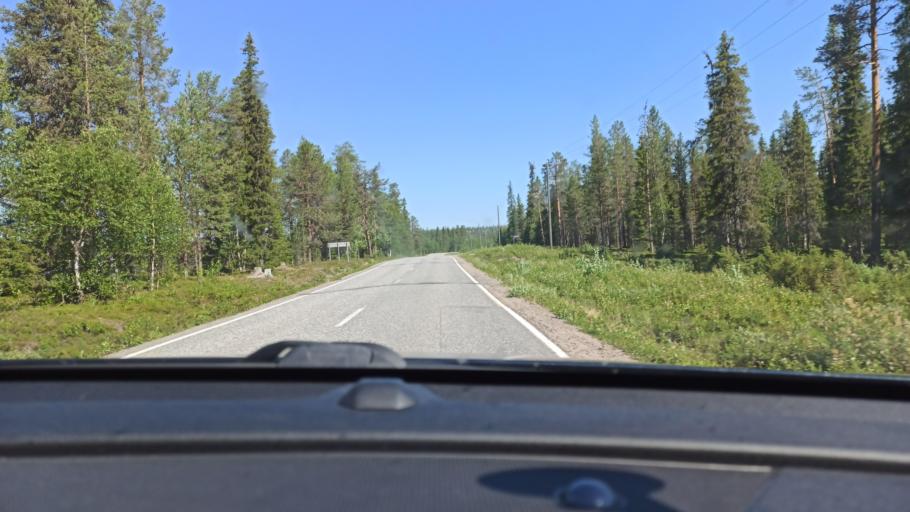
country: FI
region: Lapland
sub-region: Tunturi-Lappi
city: Kolari
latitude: 67.6273
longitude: 24.1557
